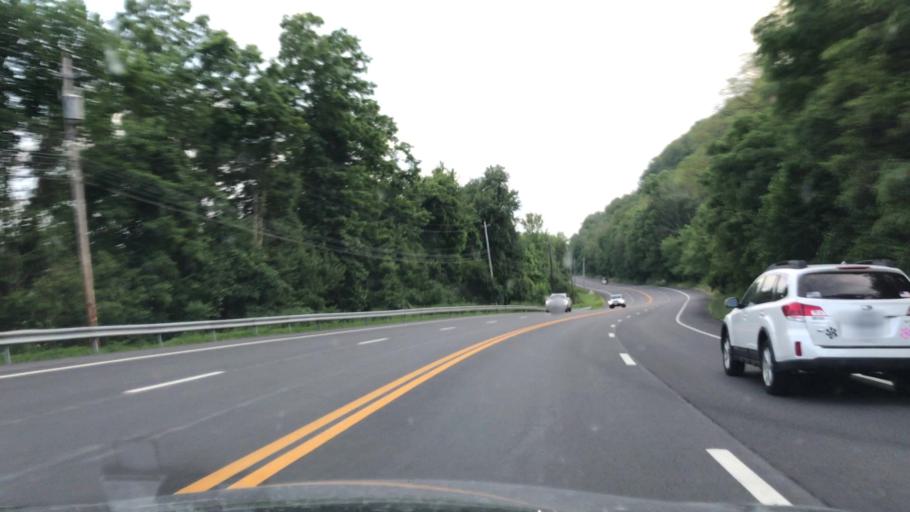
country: US
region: New York
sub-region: Orange County
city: Harriman
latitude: 41.2381
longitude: -74.1772
